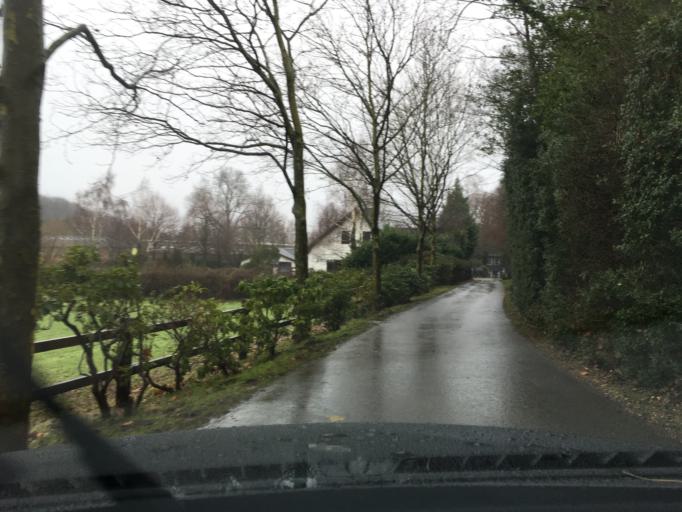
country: DE
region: North Rhine-Westphalia
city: Hattingen
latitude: 51.3804
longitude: 7.1572
